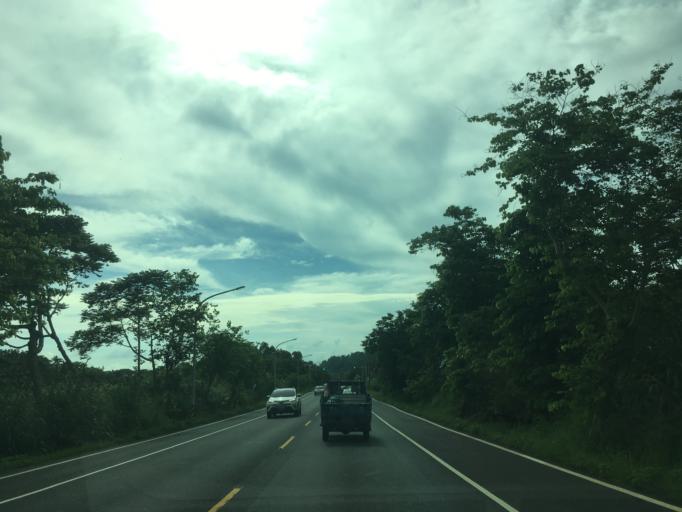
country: TW
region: Taiwan
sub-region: Chiayi
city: Jiayi Shi
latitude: 23.4506
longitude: 120.5699
